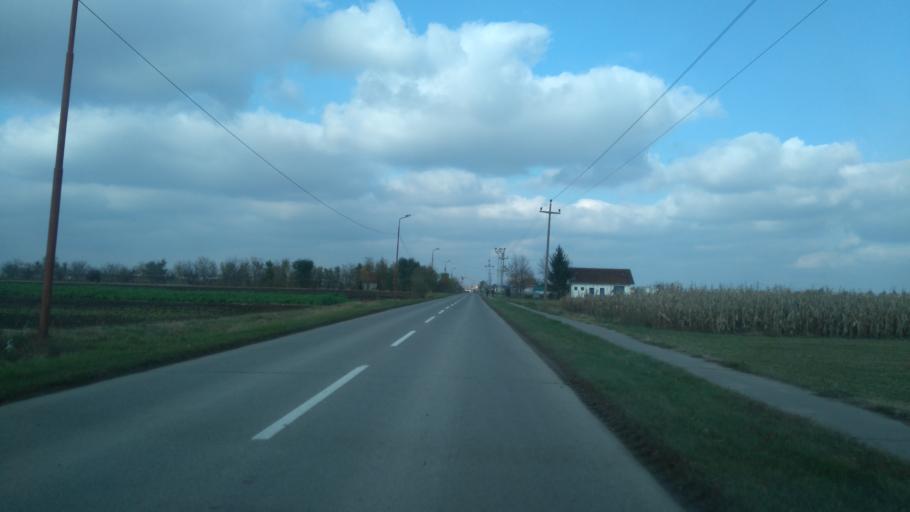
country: RS
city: Mol
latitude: 45.7768
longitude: 20.1282
